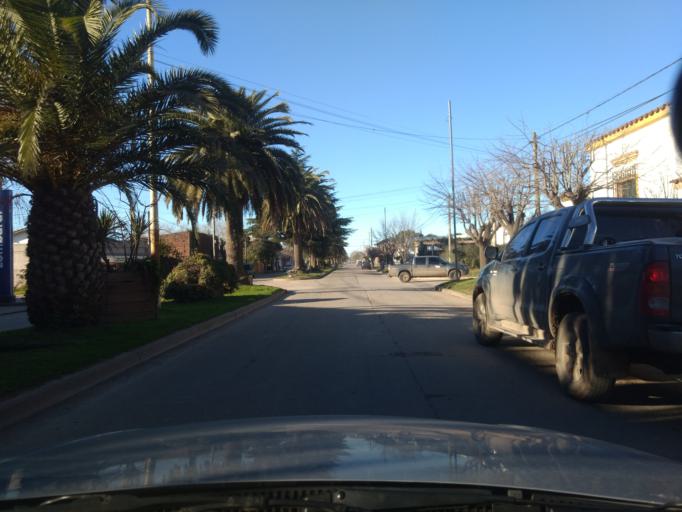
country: AR
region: Buenos Aires
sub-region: Partido de Navarro
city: Navarro
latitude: -34.9992
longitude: -59.2735
